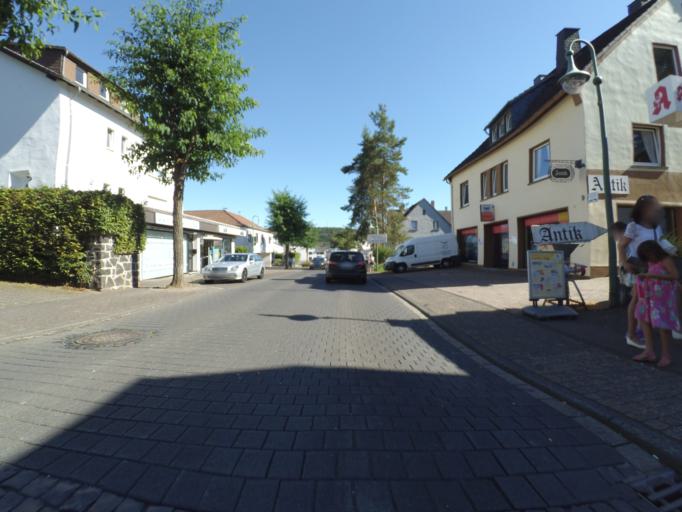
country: DE
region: Rheinland-Pfalz
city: Daun
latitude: 50.1964
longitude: 6.8285
